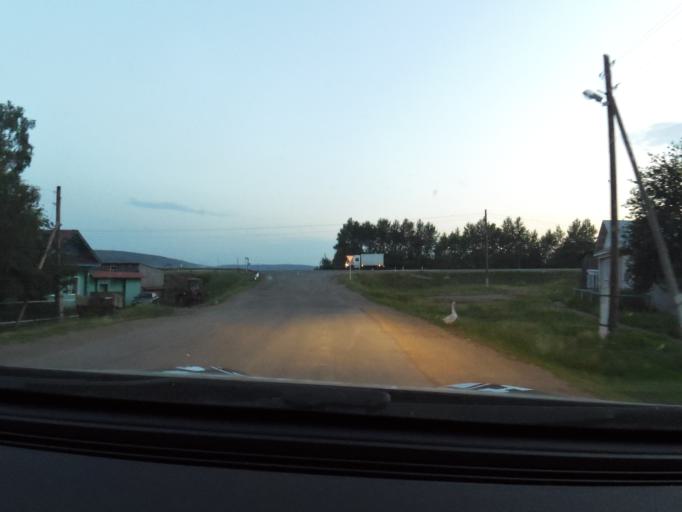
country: RU
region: Sverdlovsk
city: Sarana
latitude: 56.1344
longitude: 58.0069
